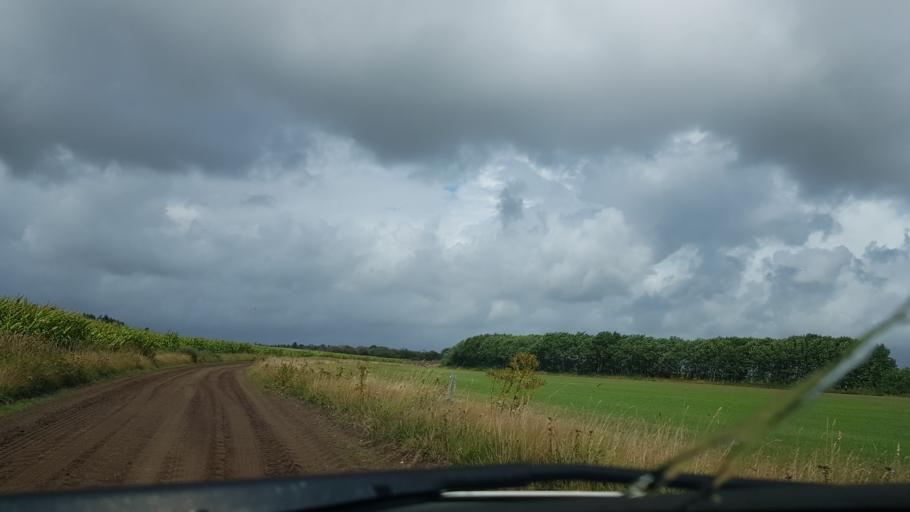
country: DK
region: South Denmark
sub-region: Esbjerg Kommune
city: Ribe
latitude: 55.2543
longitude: 8.7635
